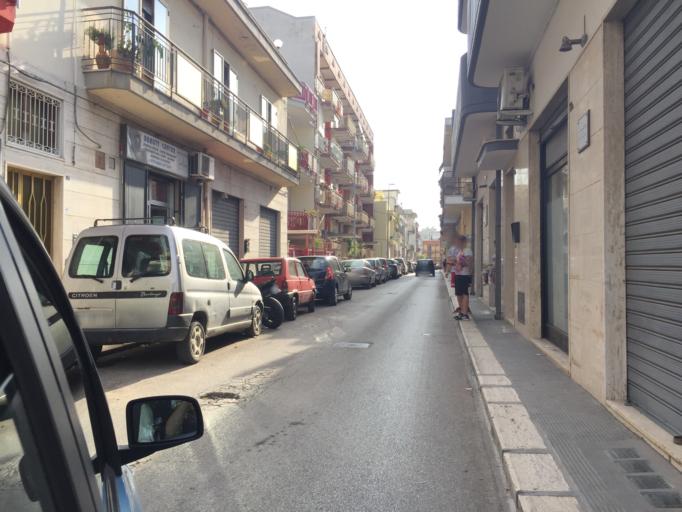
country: IT
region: Apulia
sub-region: Provincia di Bari
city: Capurso
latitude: 41.0453
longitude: 16.9212
